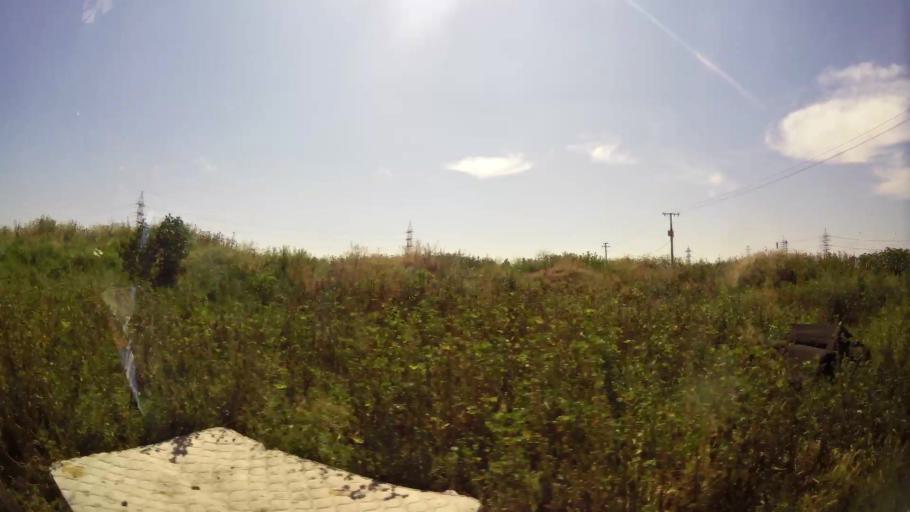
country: CL
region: Santiago Metropolitan
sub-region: Provincia de Santiago
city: Lo Prado
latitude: -33.4853
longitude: -70.7340
